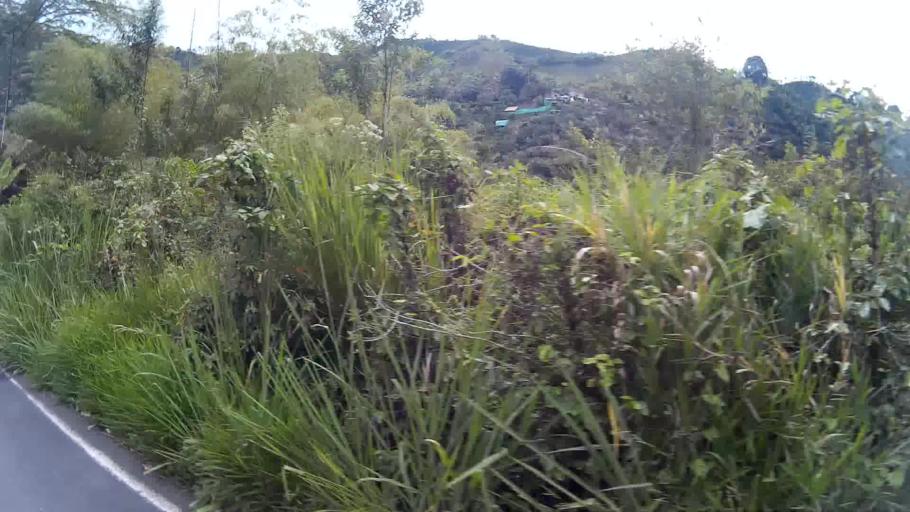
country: CO
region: Risaralda
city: Marsella
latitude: 4.8997
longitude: -75.7329
